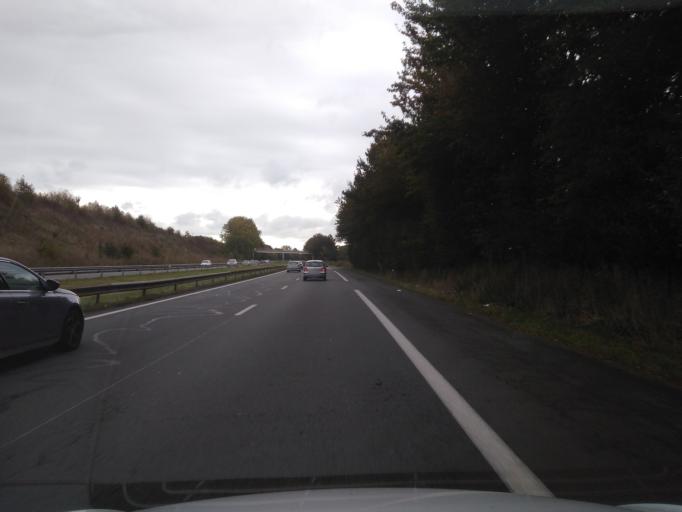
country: FR
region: Nord-Pas-de-Calais
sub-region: Departement du Nord
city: Sainghin-en-Melantois
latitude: 50.5646
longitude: 3.1636
